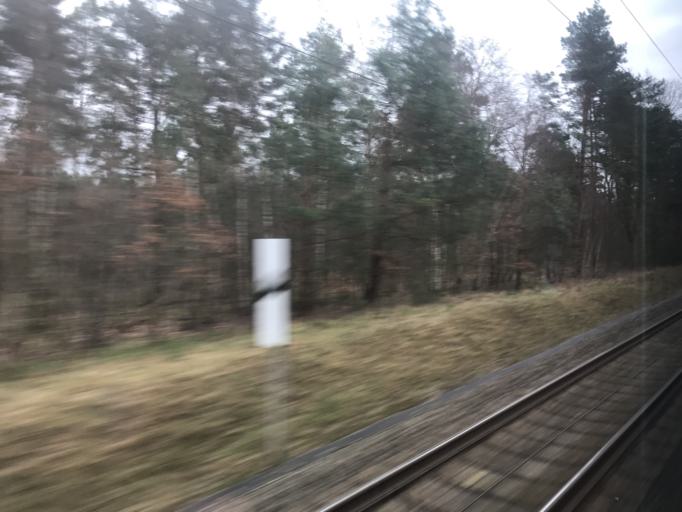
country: DE
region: Lower Saxony
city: Leiferde
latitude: 52.4567
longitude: 10.4089
